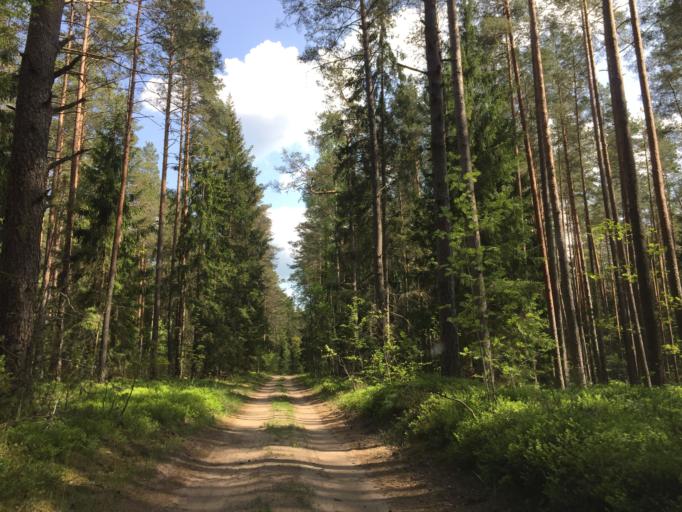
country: LV
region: Baldone
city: Baldone
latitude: 56.8005
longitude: 24.4295
